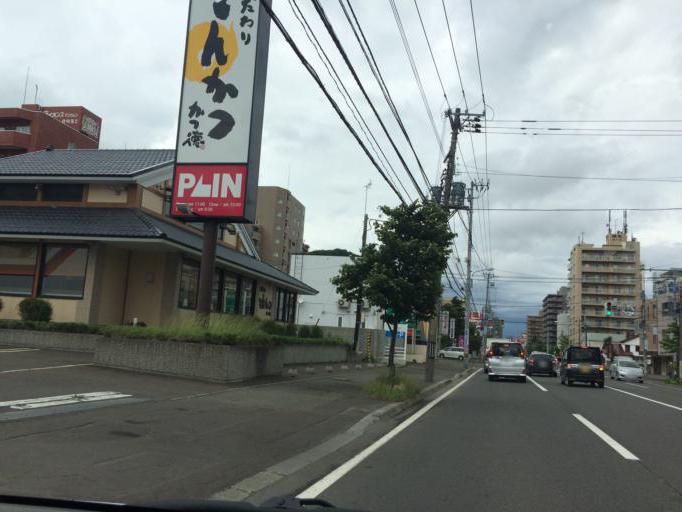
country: JP
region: Hokkaido
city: Sapporo
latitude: 43.0394
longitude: 141.3287
